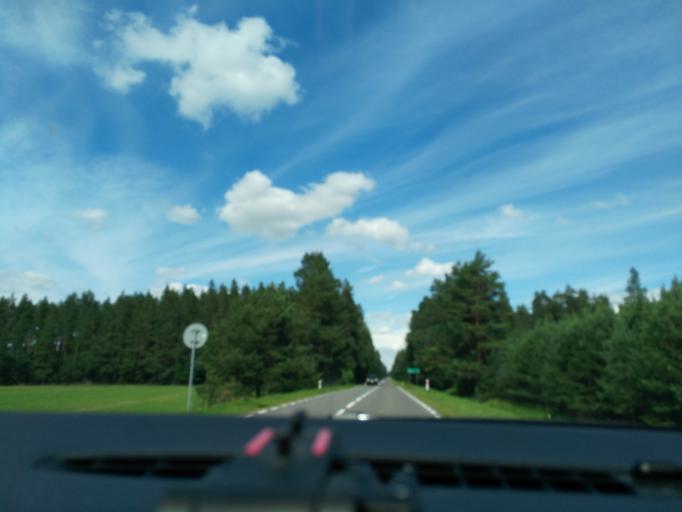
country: PL
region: Podlasie
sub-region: Powiat sejnenski
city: Sejny
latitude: 53.9843
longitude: 23.2966
